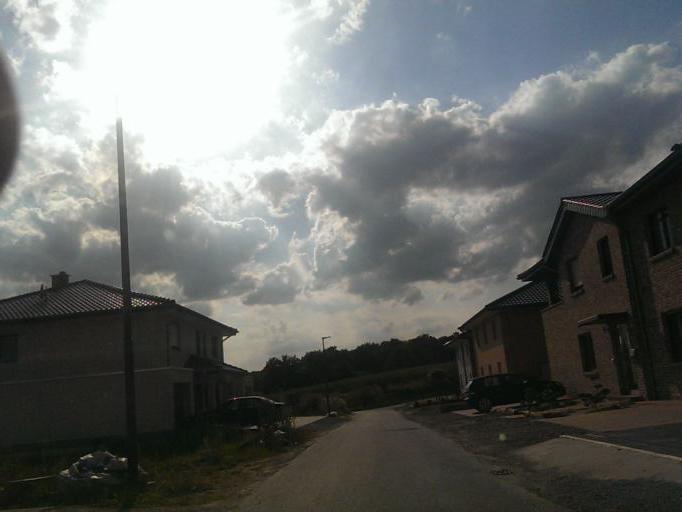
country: DE
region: North Rhine-Westphalia
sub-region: Regierungsbezirk Detmold
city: Delbruck
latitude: 51.7641
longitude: 8.5459
